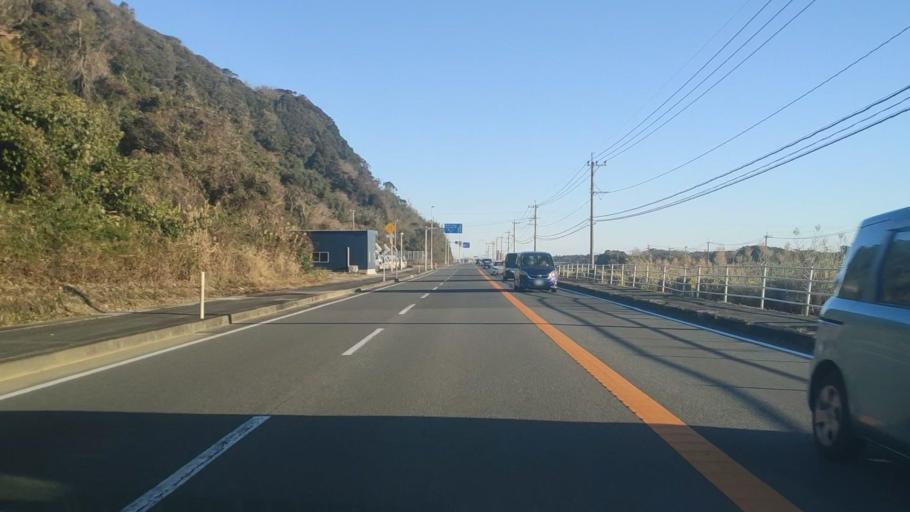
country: JP
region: Miyazaki
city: Takanabe
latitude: 32.1099
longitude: 131.5261
